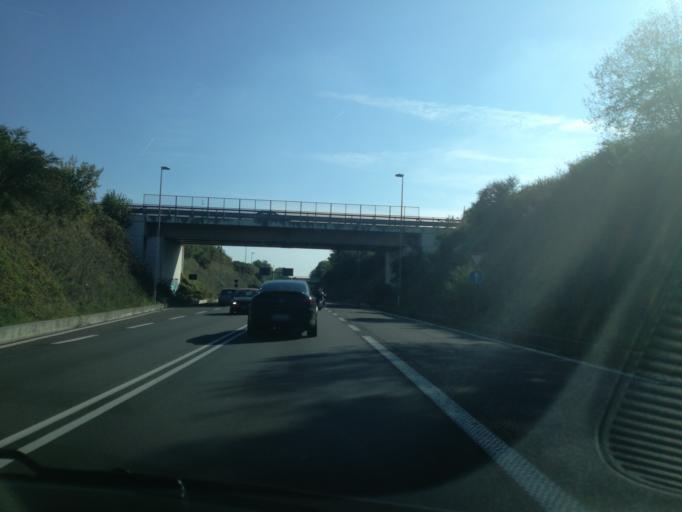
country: IT
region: Lombardy
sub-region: Provincia di Bergamo
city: Mapello
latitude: 45.7042
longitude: 9.5592
